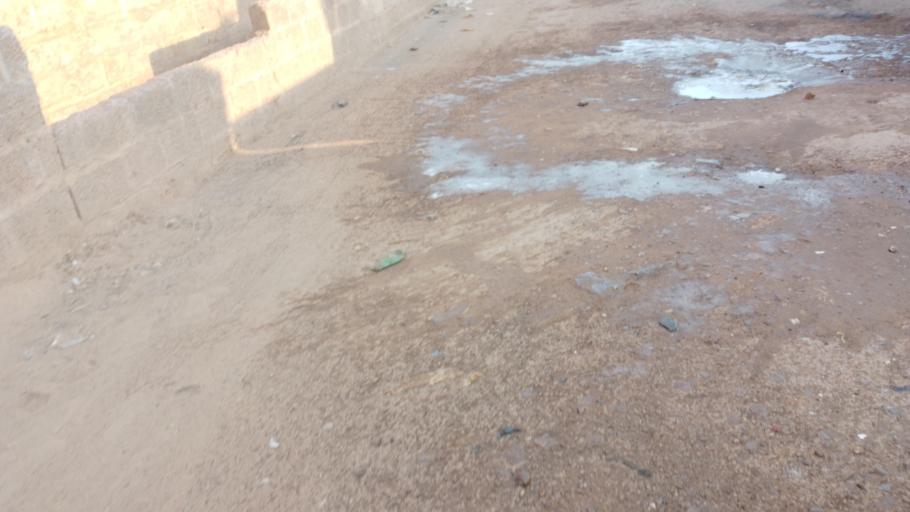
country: ZM
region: Lusaka
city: Lusaka
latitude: -15.3985
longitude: 28.3723
